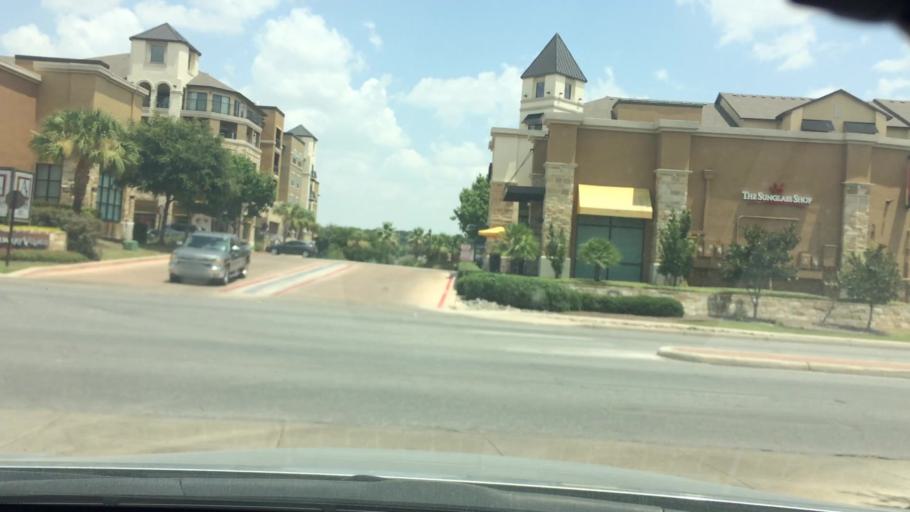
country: US
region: Texas
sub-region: Bexar County
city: Alamo Heights
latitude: 29.4956
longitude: -98.4795
